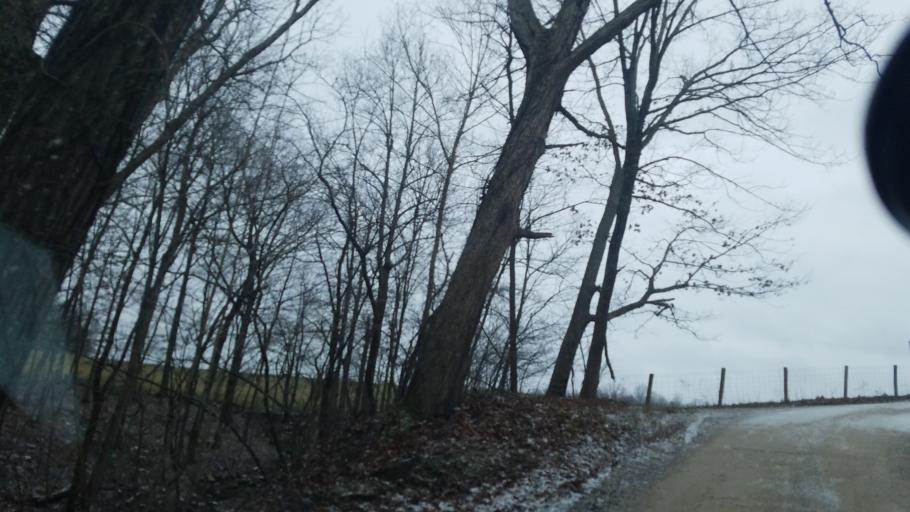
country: US
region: Kentucky
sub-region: Fleming County
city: Flemingsburg
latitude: 38.4723
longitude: -83.5119
